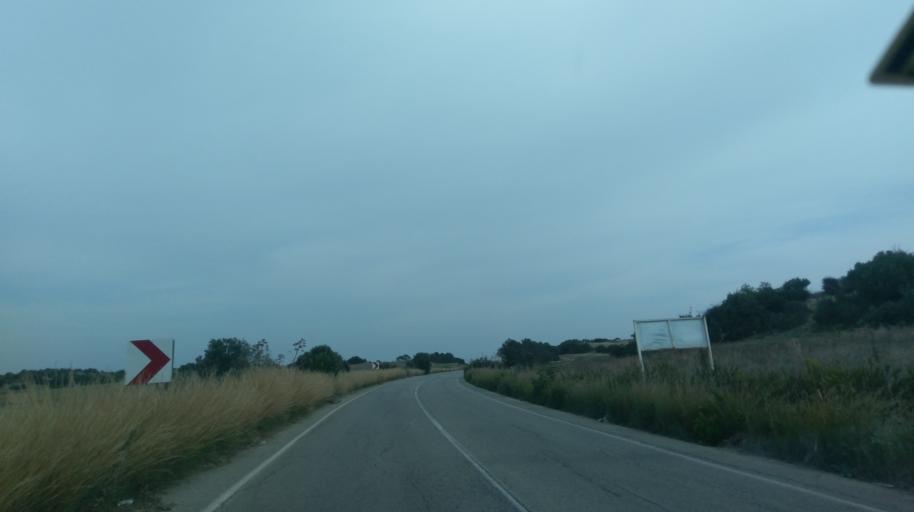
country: CY
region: Ammochostos
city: Leonarisso
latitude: 35.4022
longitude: 34.0824
